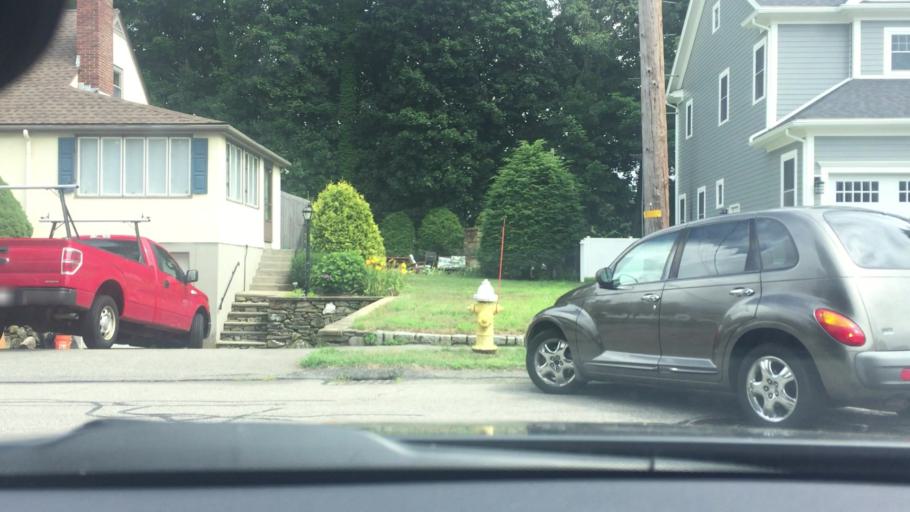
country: US
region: Massachusetts
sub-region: Norfolk County
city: Needham
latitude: 42.2986
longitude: -71.2292
